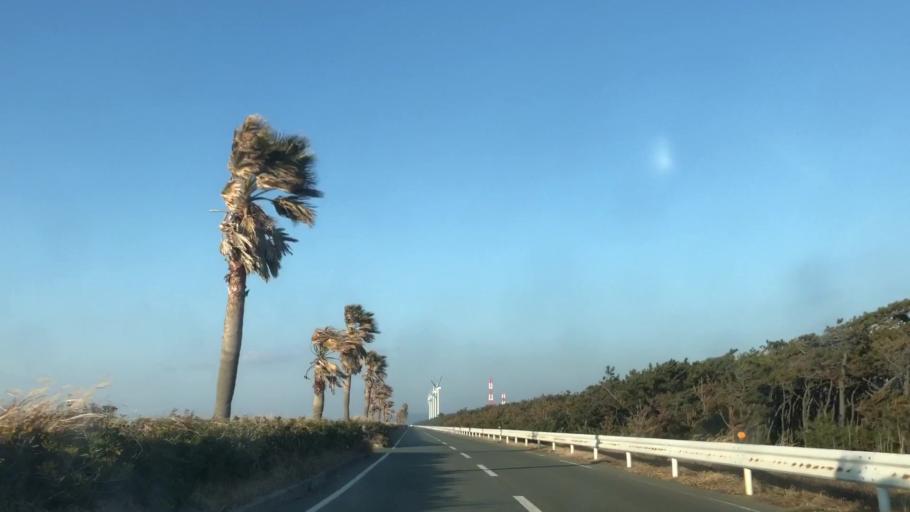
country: JP
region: Aichi
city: Toyohama
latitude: 34.6246
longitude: 137.0449
